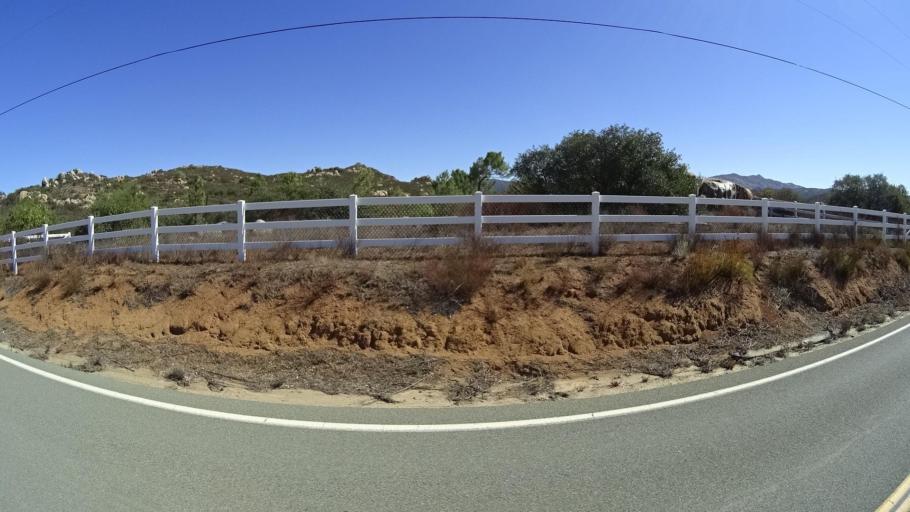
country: US
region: California
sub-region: San Diego County
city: Descanso
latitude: 32.7546
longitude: -116.6756
